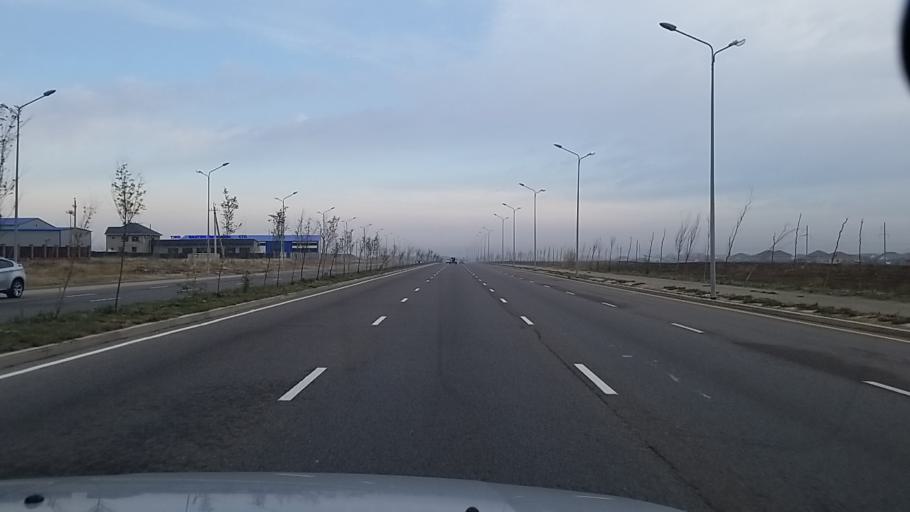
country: KZ
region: Almaty Oblysy
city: Burunday
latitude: 43.3374
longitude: 76.8336
